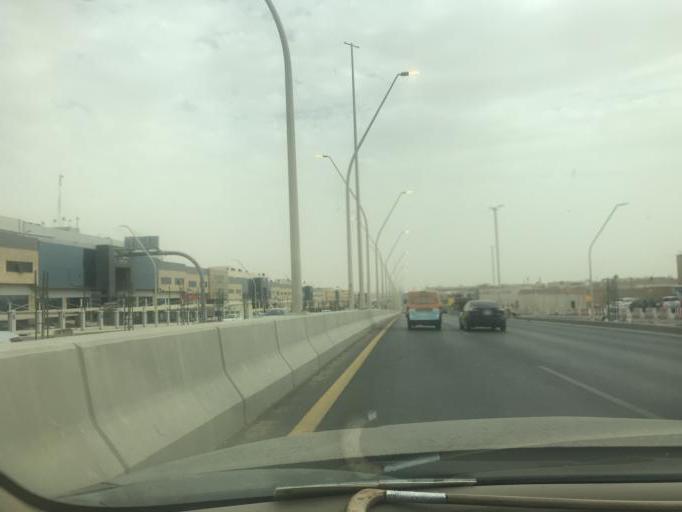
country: SA
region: Ar Riyad
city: Riyadh
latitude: 24.8174
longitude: 46.6662
